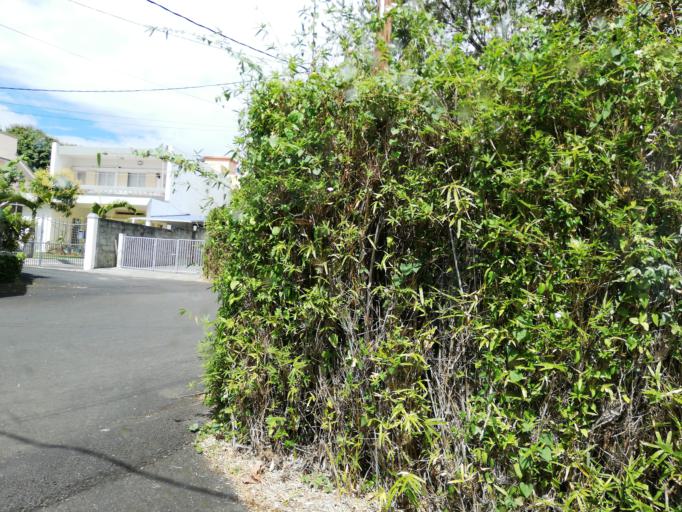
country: MU
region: Moka
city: Moka
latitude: -20.2186
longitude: 57.4720
